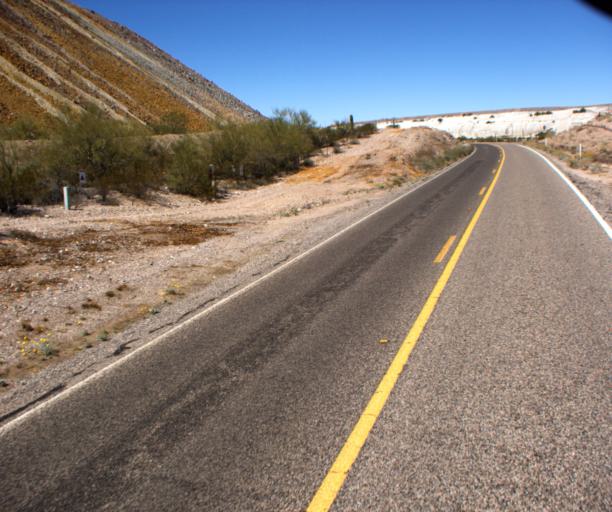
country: US
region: Arizona
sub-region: Pima County
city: Ajo
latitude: 32.3654
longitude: -112.8382
